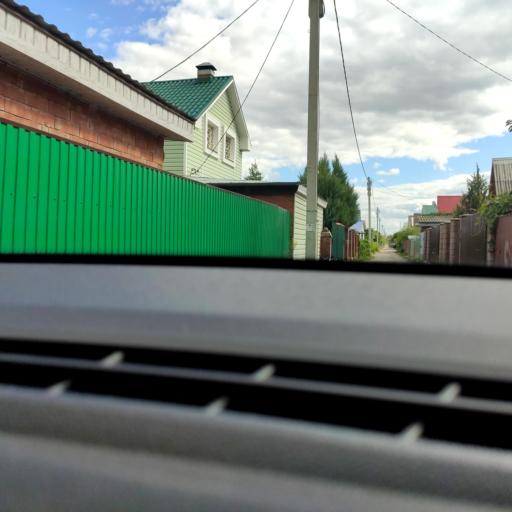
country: RU
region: Samara
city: Podstepki
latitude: 53.5845
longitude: 49.0752
